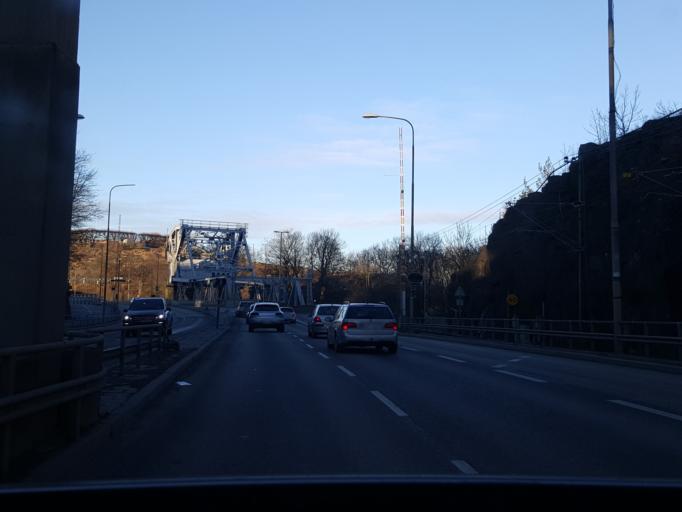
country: SE
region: Stockholm
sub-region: Stockholms Kommun
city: OEstermalm
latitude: 59.3129
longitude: 18.1067
